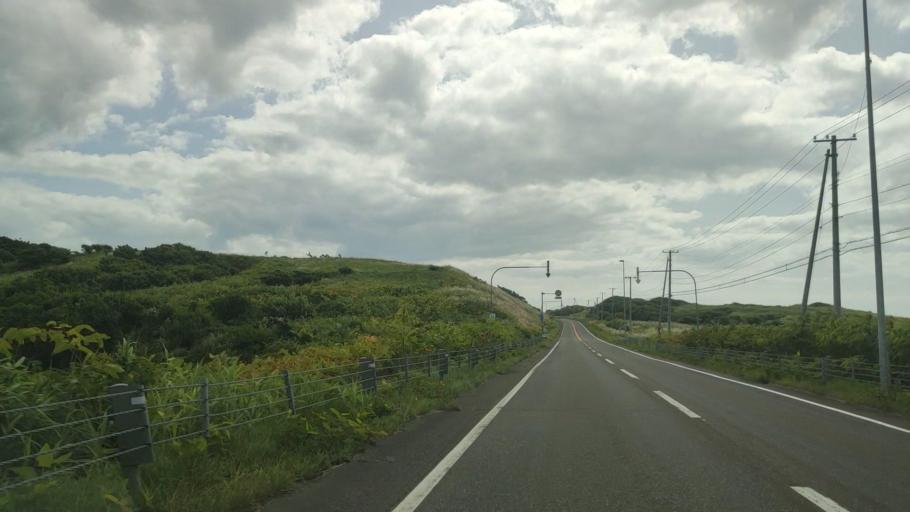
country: JP
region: Hokkaido
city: Rumoi
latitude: 44.5926
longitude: 141.7905
